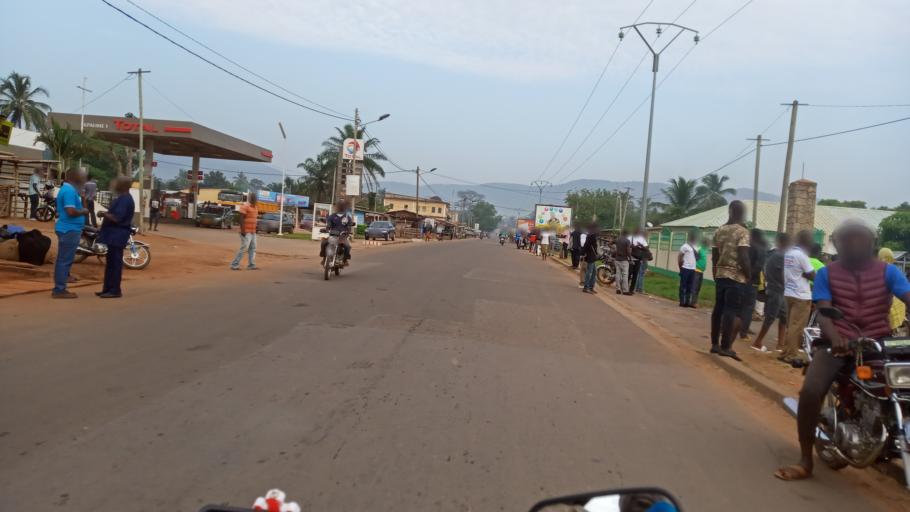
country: TG
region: Plateaux
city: Kpalime
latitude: 6.8987
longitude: 0.6360
